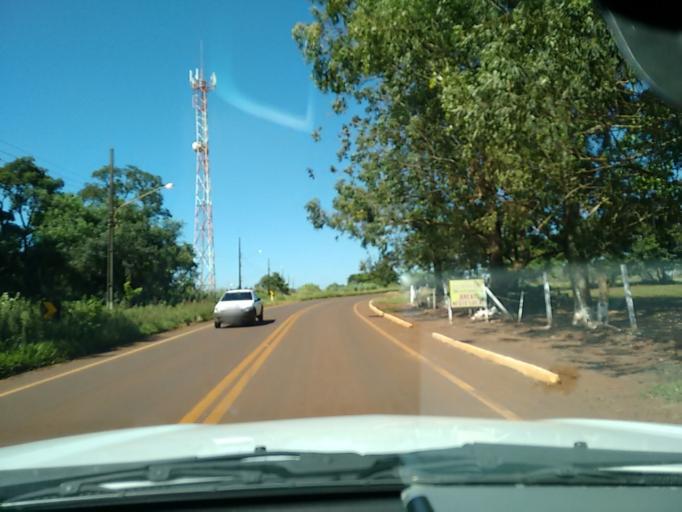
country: BR
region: Mato Grosso do Sul
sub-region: Maracaju
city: Maracaju
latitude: -22.0904
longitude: -55.3538
